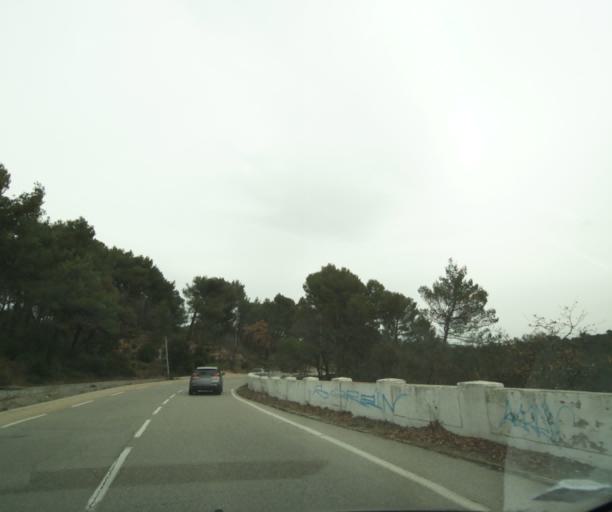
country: FR
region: Provence-Alpes-Cote d'Azur
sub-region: Departement des Bouches-du-Rhone
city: Peynier
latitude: 43.4313
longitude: 5.6242
